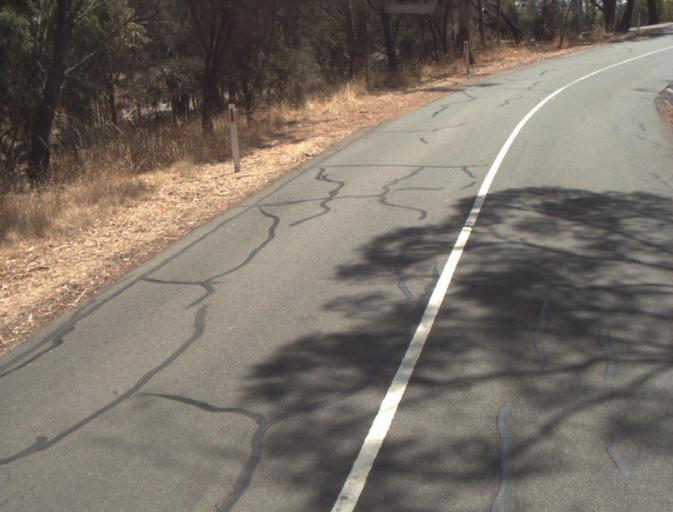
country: AU
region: Tasmania
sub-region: Launceston
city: West Launceston
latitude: -41.4500
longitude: 147.1198
